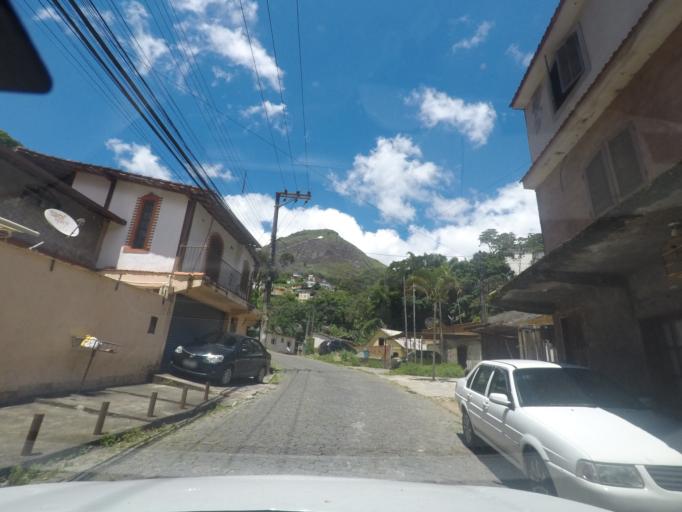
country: BR
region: Rio de Janeiro
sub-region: Teresopolis
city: Teresopolis
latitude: -22.4226
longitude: -42.9841
